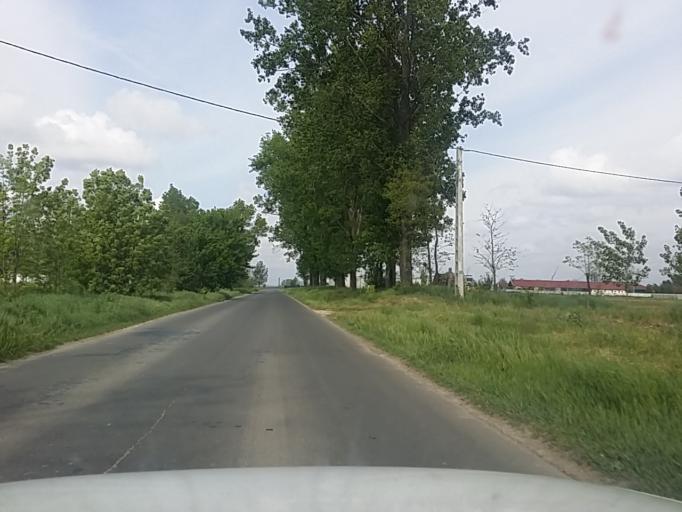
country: HU
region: Pest
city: Szentlorinckata
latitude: 47.5108
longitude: 19.7511
